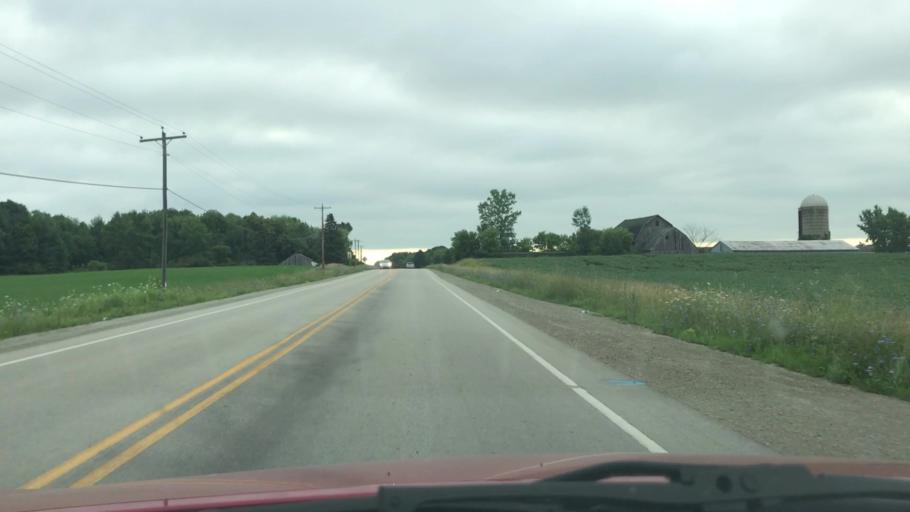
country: US
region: Wisconsin
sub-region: Brown County
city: De Pere
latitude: 44.4297
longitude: -88.1342
